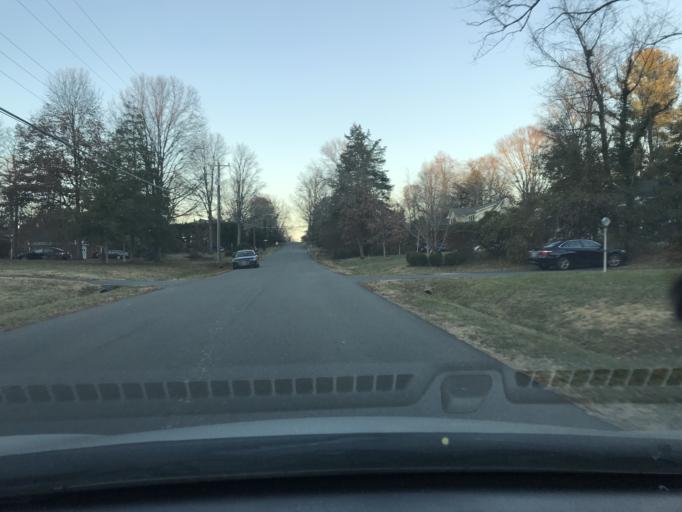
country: US
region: Virginia
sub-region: City of Fairfax
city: Fairfax
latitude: 38.8625
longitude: -77.3131
